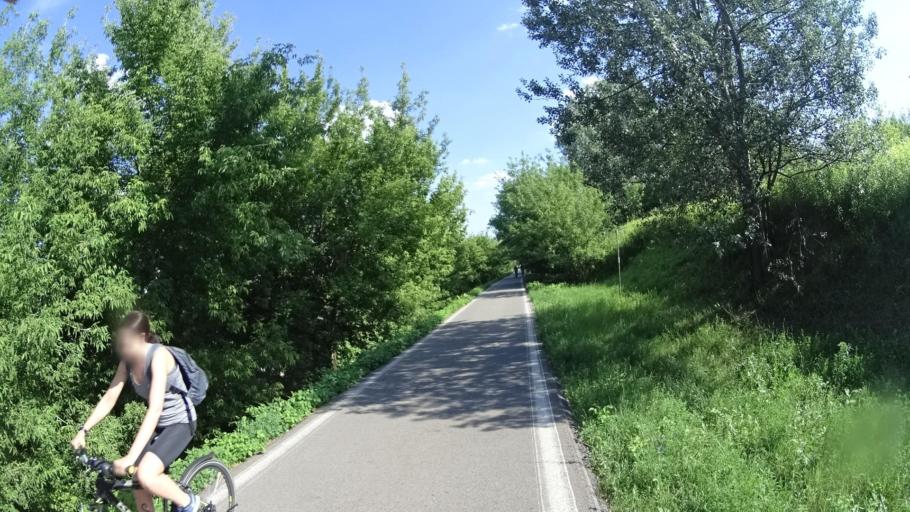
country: PL
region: Masovian Voivodeship
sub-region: Warszawa
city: Bialoleka
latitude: 52.3003
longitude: 20.9756
